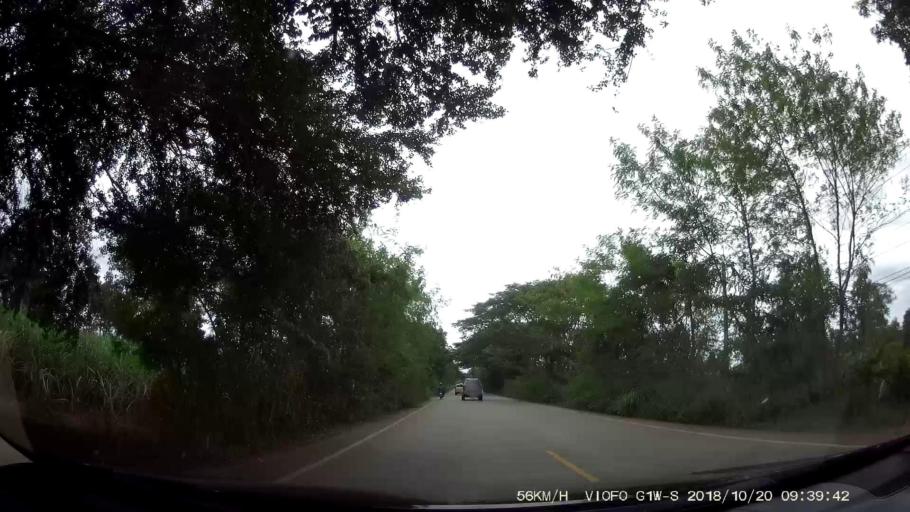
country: TH
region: Chaiyaphum
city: Kaset Sombun
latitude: 16.4367
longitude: 101.9642
